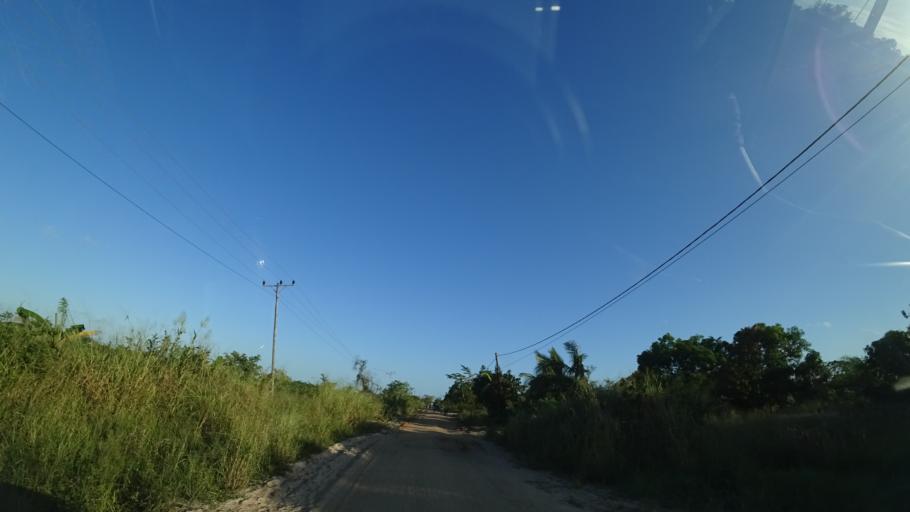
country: MZ
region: Sofala
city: Dondo
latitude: -19.3914
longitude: 34.7085
